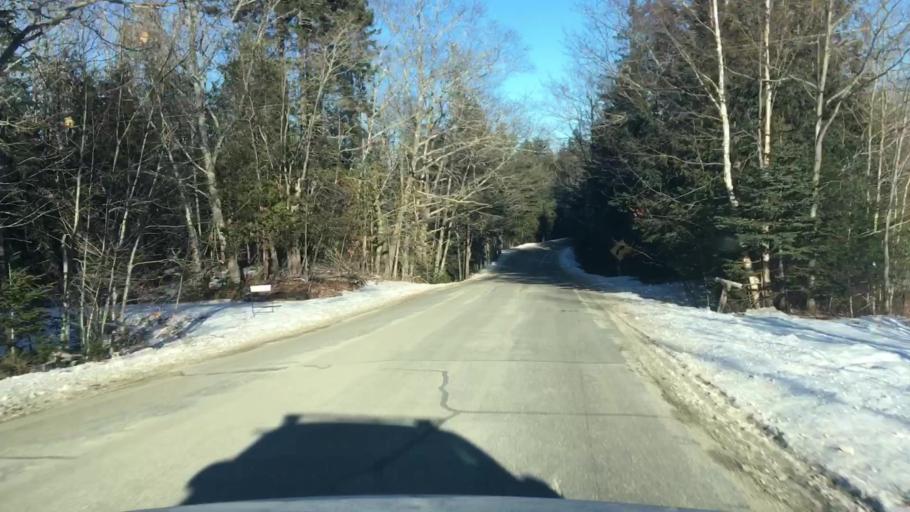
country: US
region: Maine
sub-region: Hancock County
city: Castine
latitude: 44.3568
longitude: -68.7772
